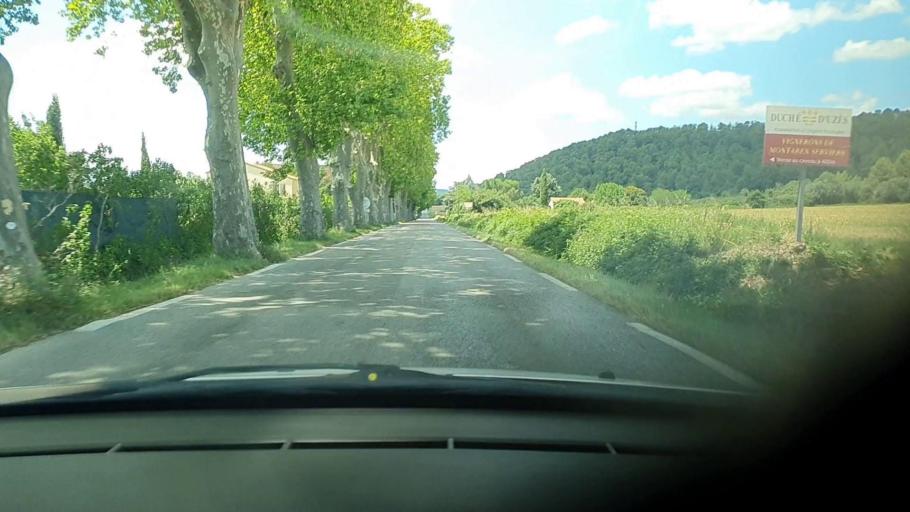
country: FR
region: Languedoc-Roussillon
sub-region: Departement du Gard
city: Montaren-et-Saint-Mediers
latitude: 44.0297
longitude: 4.3761
